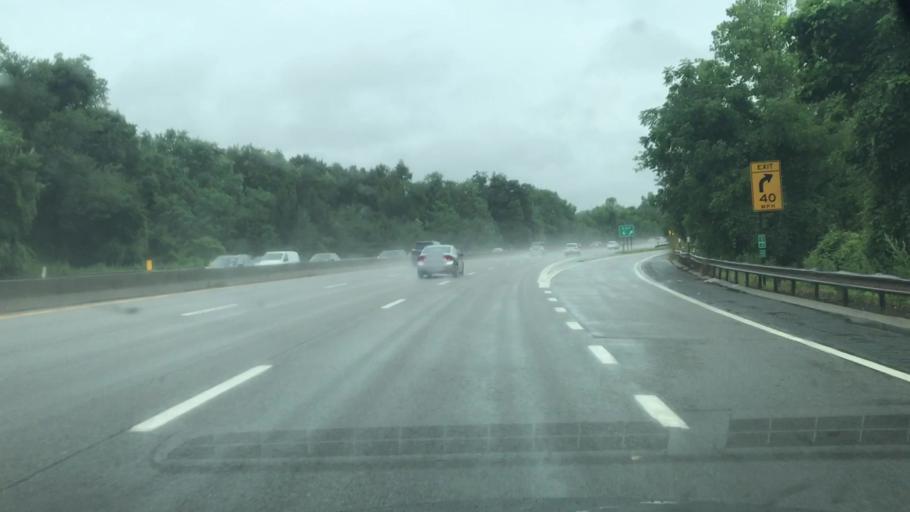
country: US
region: New York
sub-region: Westchester County
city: Briarcliff Manor
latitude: 41.1400
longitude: -73.8170
